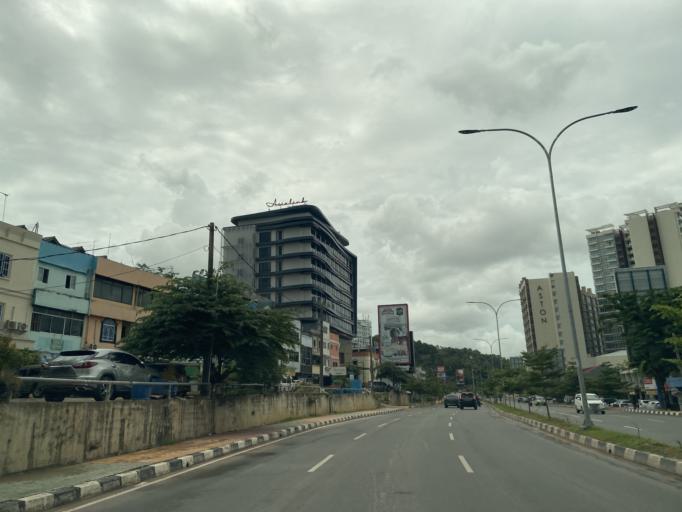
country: SG
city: Singapore
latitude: 1.1447
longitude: 104.0187
